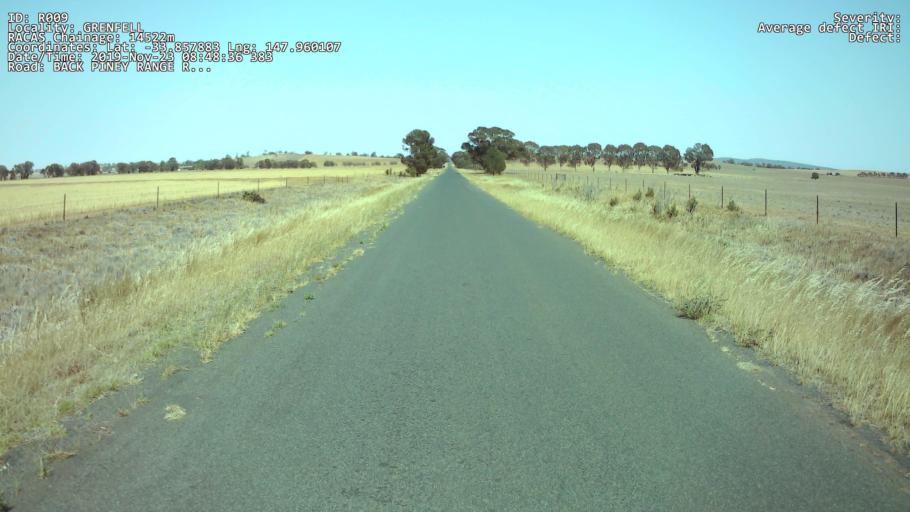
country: AU
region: New South Wales
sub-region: Weddin
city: Grenfell
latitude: -33.8579
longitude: 147.9601
